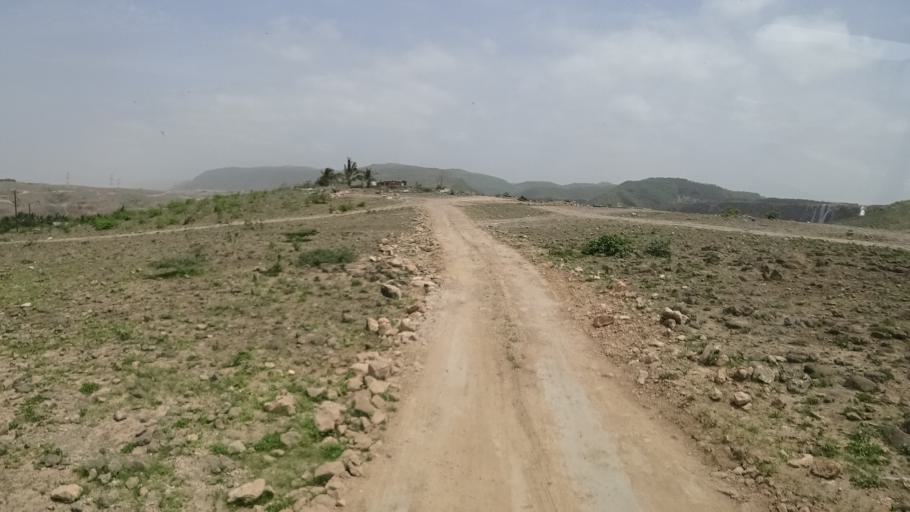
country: OM
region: Zufar
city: Salalah
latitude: 17.0656
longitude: 54.4363
